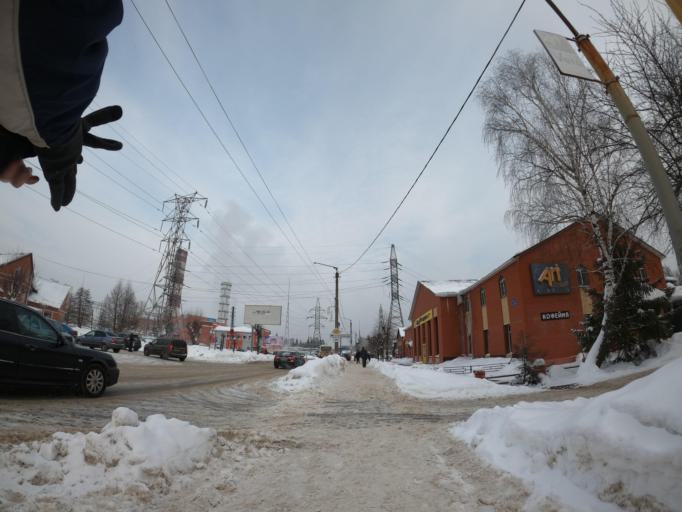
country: RU
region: Moskovskaya
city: Elektrogorsk
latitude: 55.8839
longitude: 38.7856
